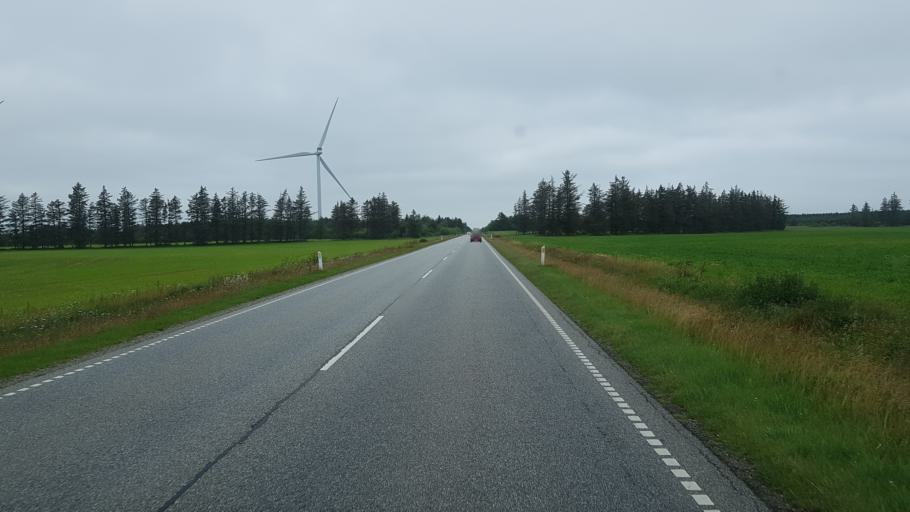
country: DK
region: Central Jutland
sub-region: Lemvig Kommune
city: Lemvig
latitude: 56.4459
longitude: 8.3570
